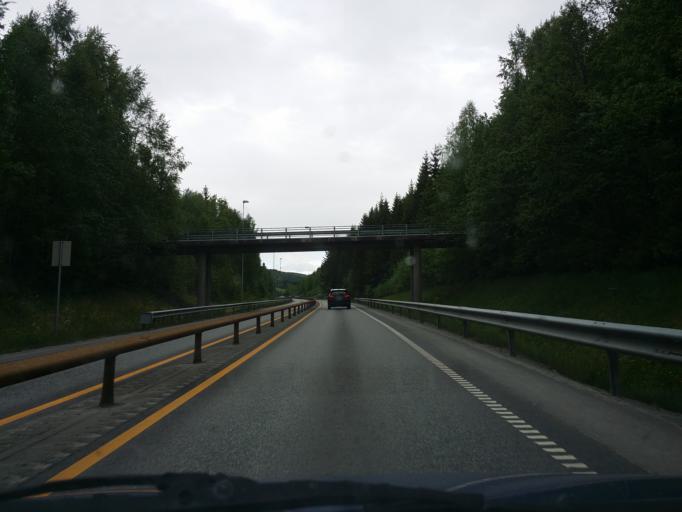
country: NO
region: Hedmark
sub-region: Ringsaker
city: Moelv
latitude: 60.9099
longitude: 10.7457
